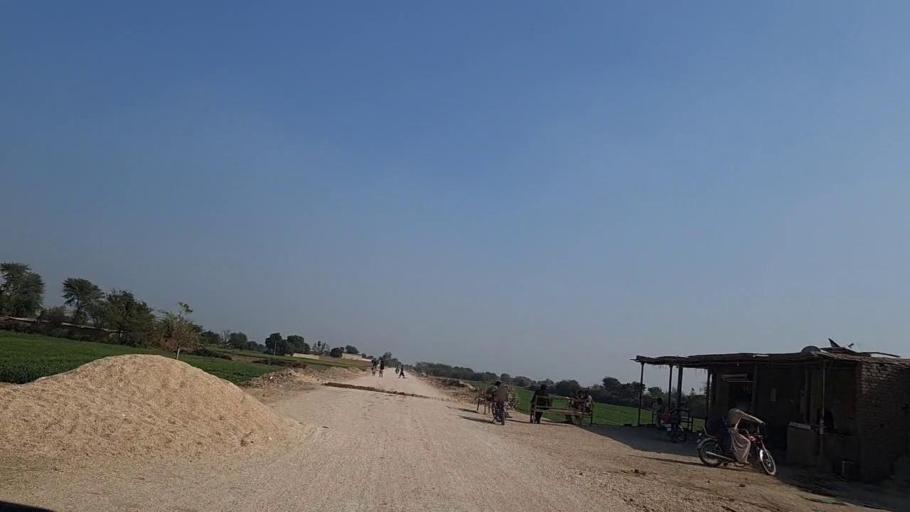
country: PK
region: Sindh
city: Sakrand
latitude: 26.0579
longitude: 68.2894
